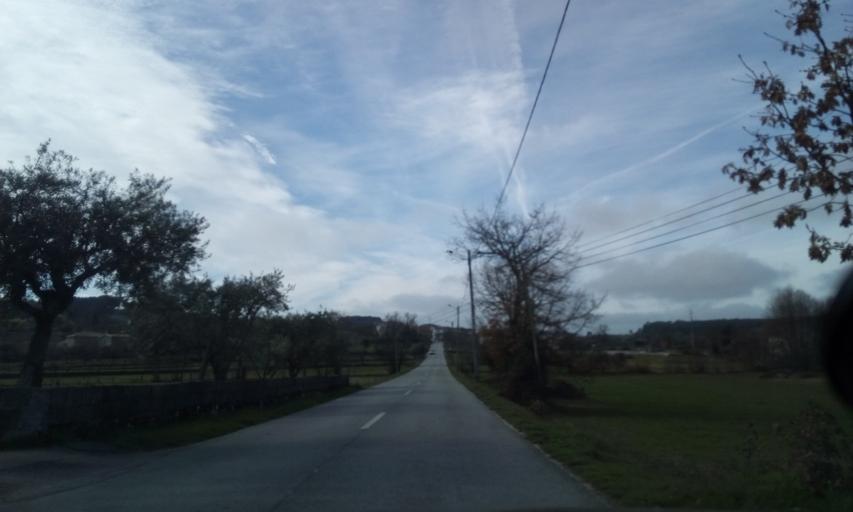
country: PT
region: Guarda
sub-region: Fornos de Algodres
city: Fornos de Algodres
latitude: 40.6610
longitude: -7.5322
